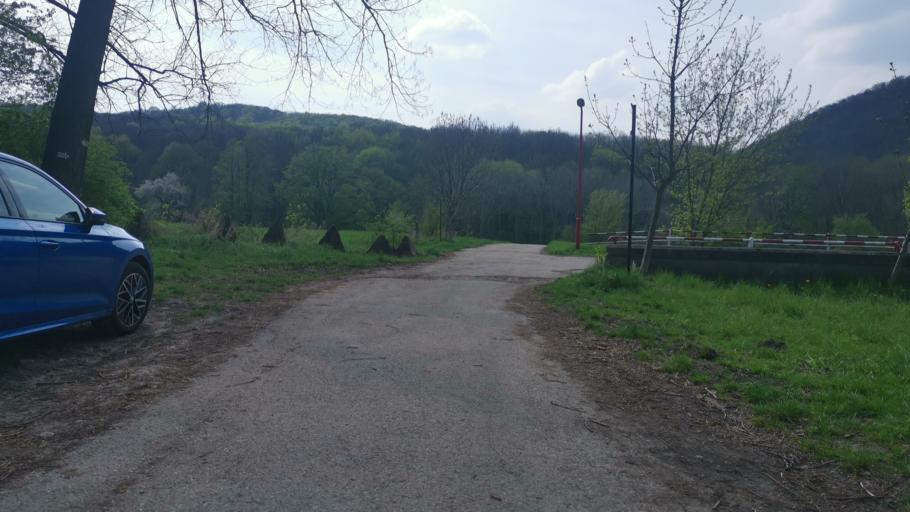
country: SK
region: Trnavsky
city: Smolenice
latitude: 48.5312
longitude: 17.3571
